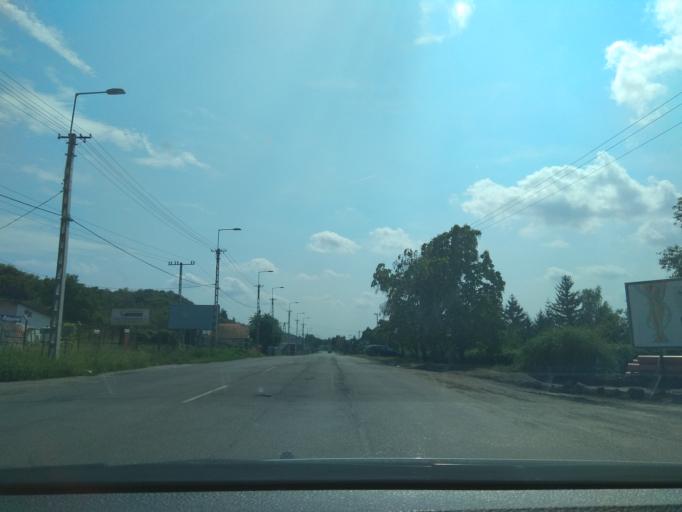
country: HU
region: Heves
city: Andornaktalya
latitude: 47.8778
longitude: 20.4003
